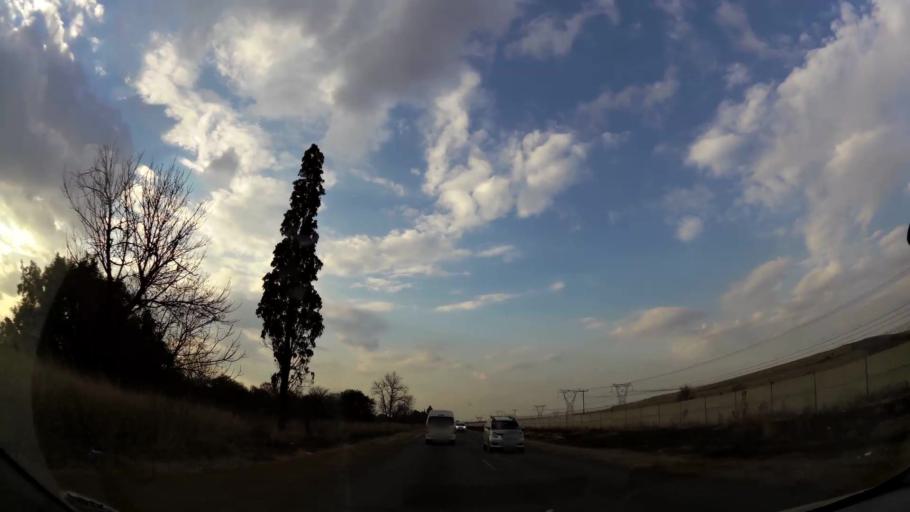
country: ZA
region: Gauteng
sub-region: Sedibeng District Municipality
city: Vanderbijlpark
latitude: -26.6424
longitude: 27.8051
